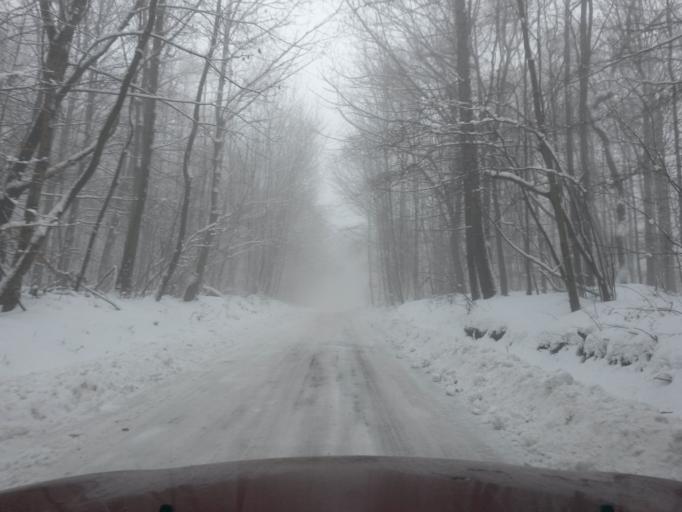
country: SK
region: Kosicky
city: Secovce
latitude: 48.8127
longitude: 21.5269
